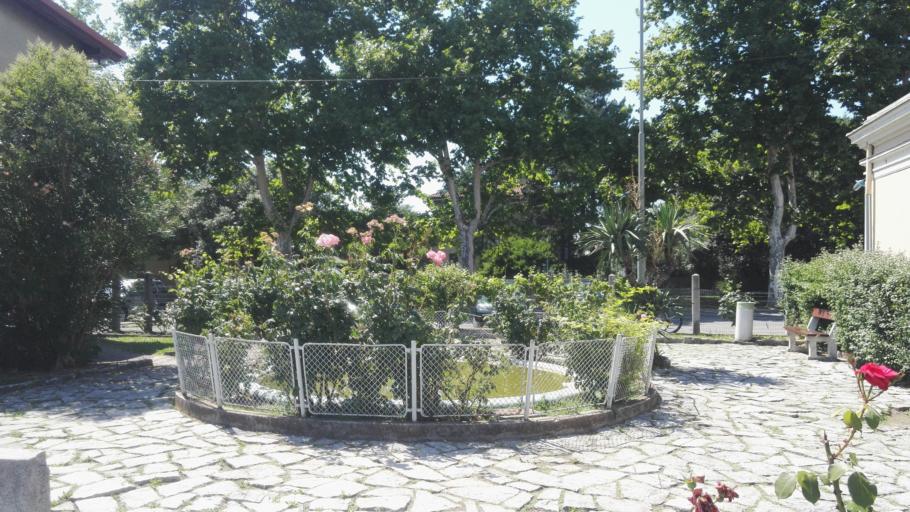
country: SI
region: Nova Gorica
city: Nova Gorica
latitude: 45.9546
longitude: 13.6352
